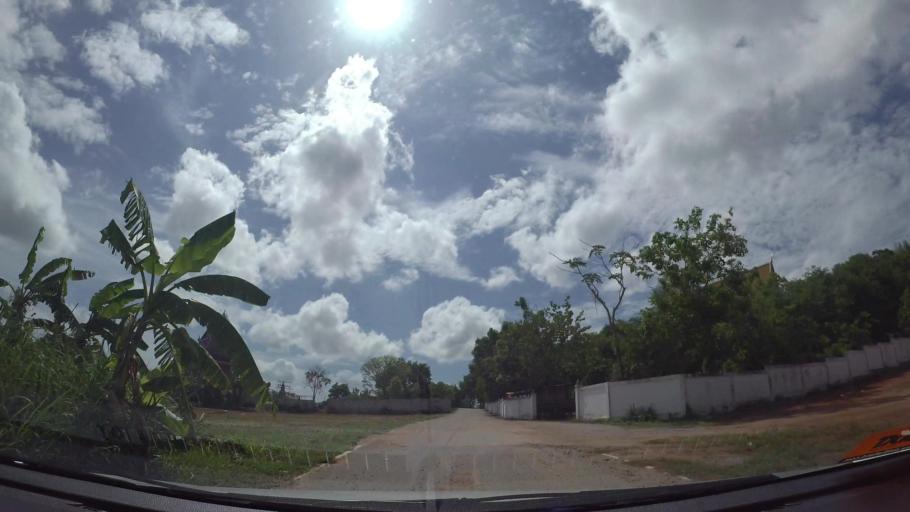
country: TH
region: Chon Buri
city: Sattahip
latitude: 12.6926
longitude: 100.9041
